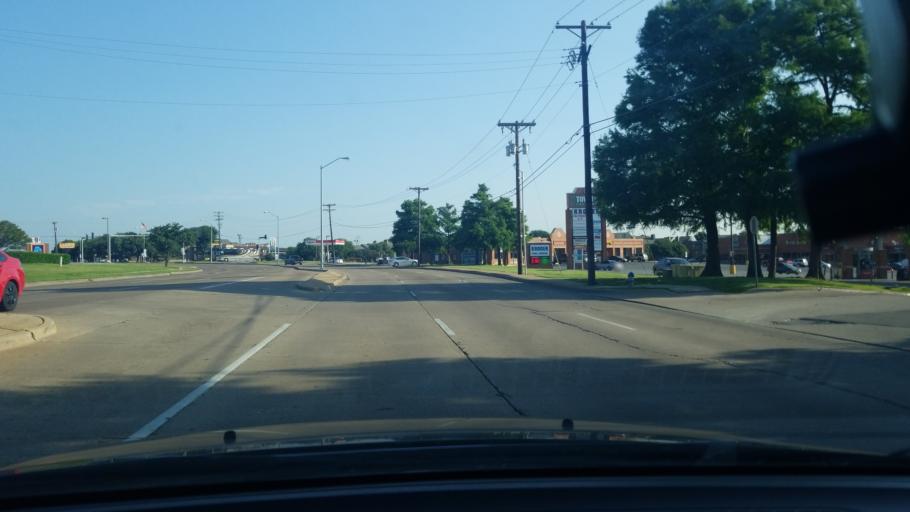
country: US
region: Texas
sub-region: Dallas County
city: Mesquite
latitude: 32.8131
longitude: -96.6349
